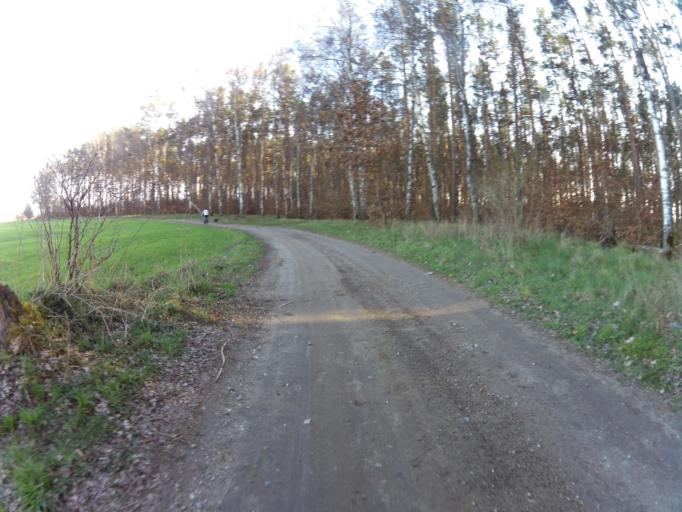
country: PL
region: West Pomeranian Voivodeship
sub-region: Powiat pyrzycki
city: Lipiany
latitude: 52.9557
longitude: 14.9294
